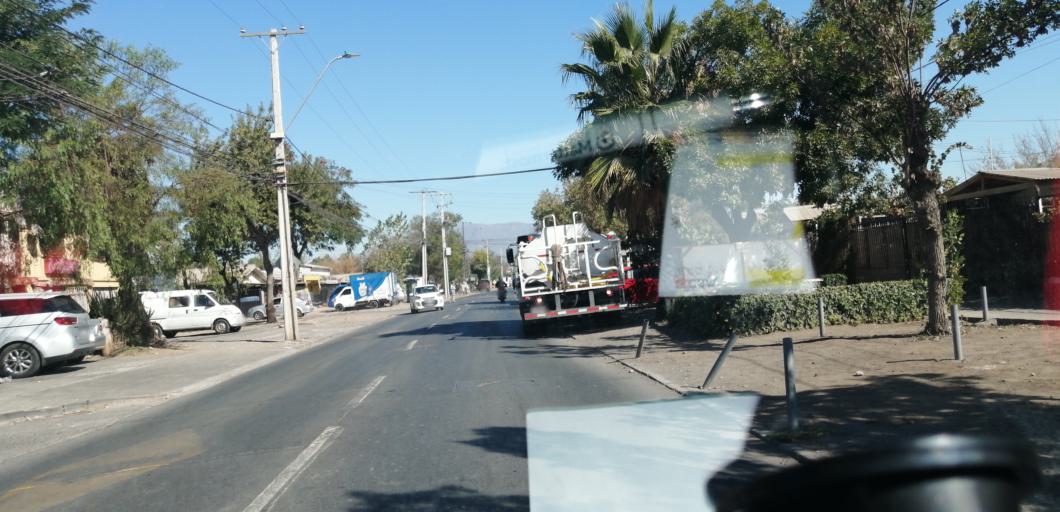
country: CL
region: Santiago Metropolitan
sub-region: Provincia de Santiago
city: Lo Prado
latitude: -33.4362
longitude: -70.7550
